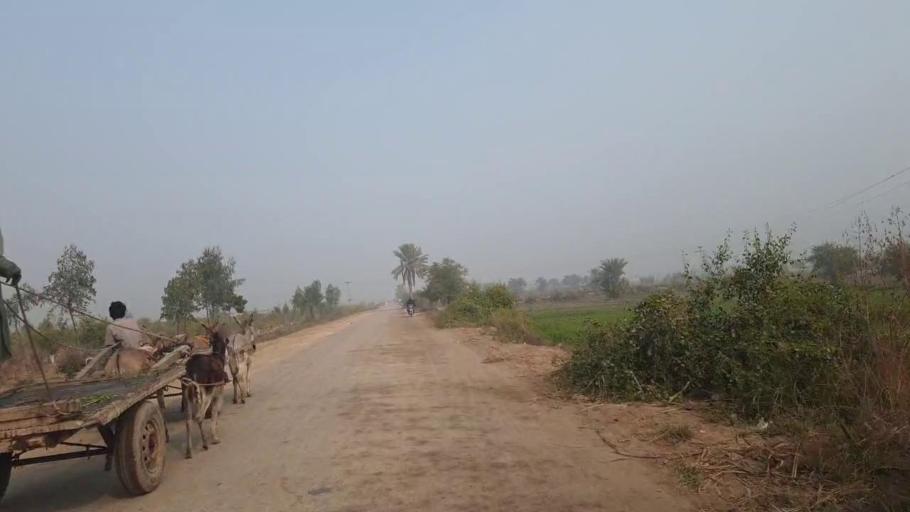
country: PK
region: Sindh
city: Tando Adam
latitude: 25.7928
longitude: 68.6103
